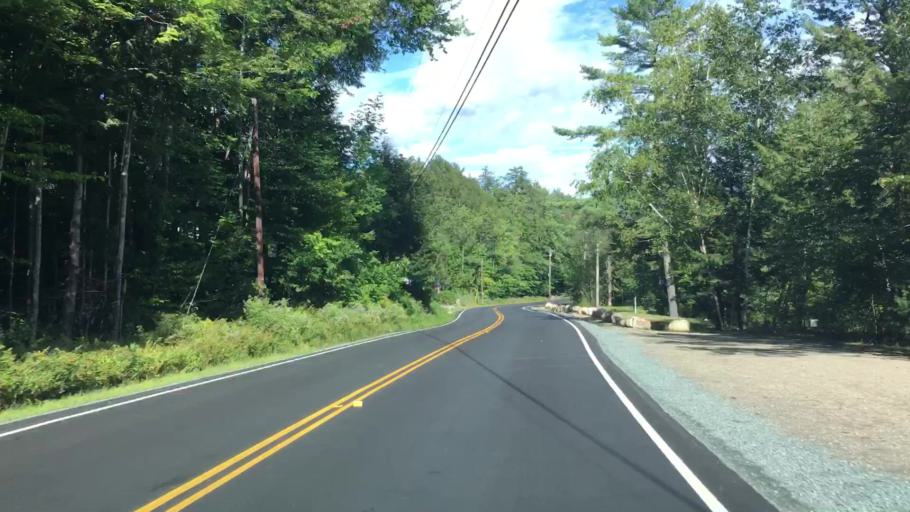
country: US
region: New Hampshire
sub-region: Grafton County
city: Woodstock
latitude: 44.0286
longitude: -71.7193
